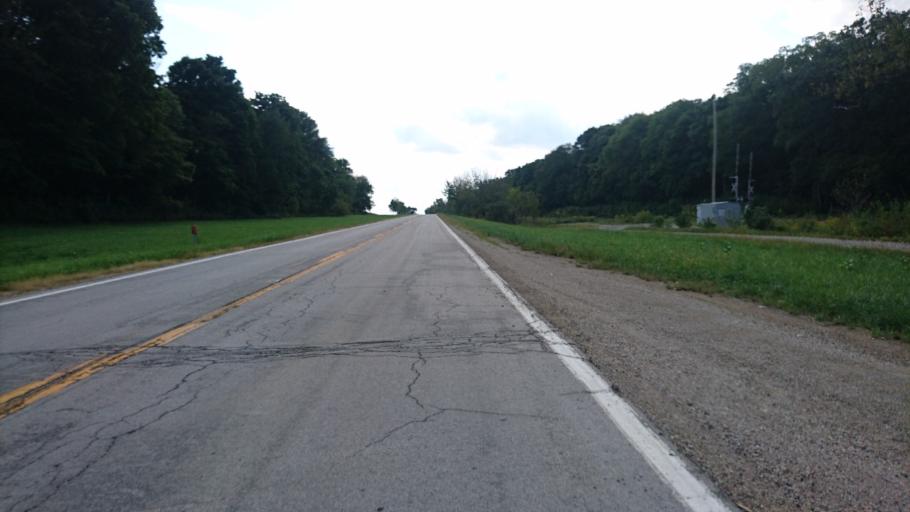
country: US
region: Illinois
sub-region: McLean County
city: Twin Grove
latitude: 40.3575
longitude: -89.1190
